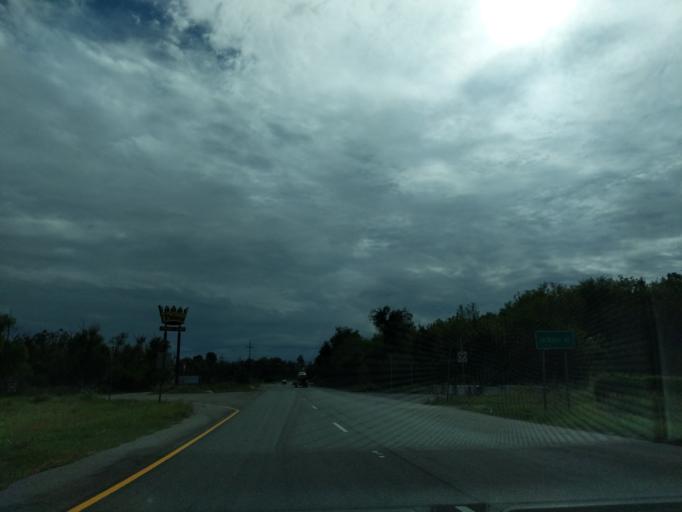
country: US
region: Louisiana
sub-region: Saint Bernard Parish
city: Chalmette
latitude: 30.0150
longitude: -89.9451
